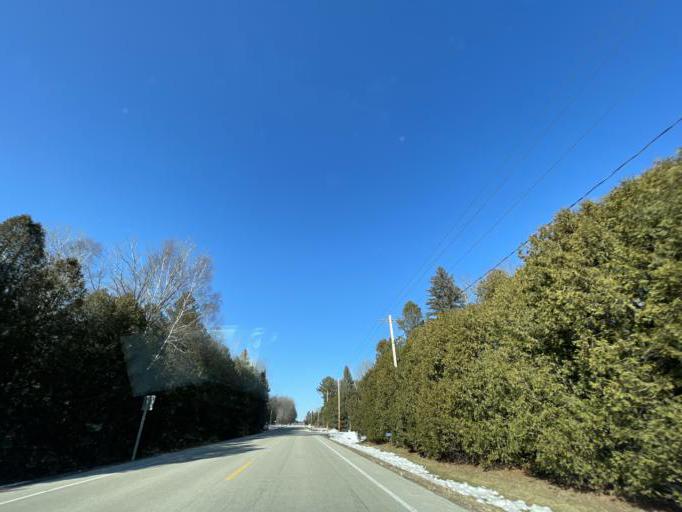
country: US
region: Wisconsin
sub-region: Brown County
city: Suamico
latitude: 44.6508
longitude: -88.0902
